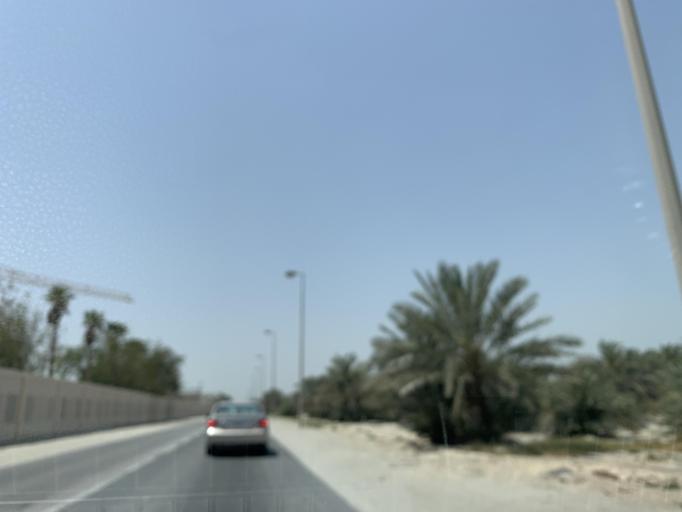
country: BH
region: Manama
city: Jidd Hafs
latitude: 26.1967
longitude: 50.5526
